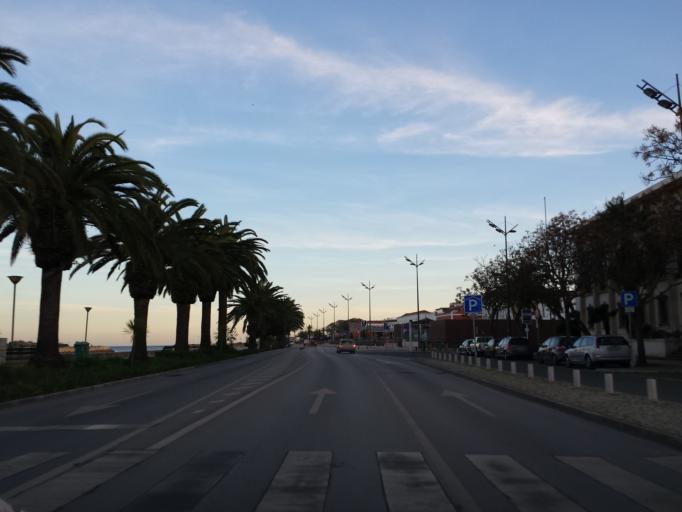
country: PT
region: Faro
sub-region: Lagos
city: Lagos
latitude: 37.1031
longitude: -8.6721
